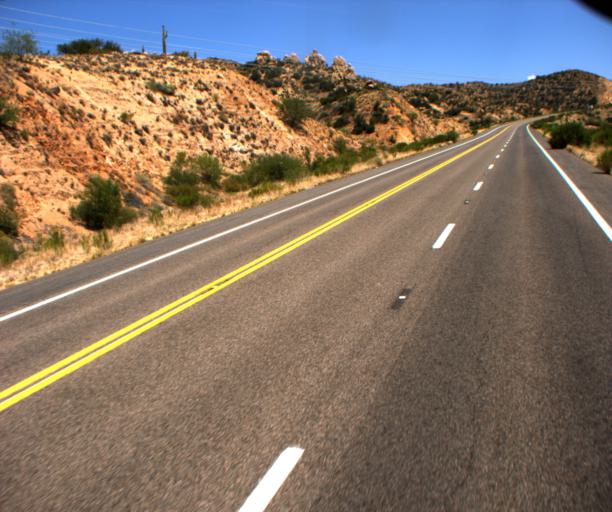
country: US
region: Arizona
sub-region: Gila County
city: Miami
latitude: 33.5466
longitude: -110.9430
